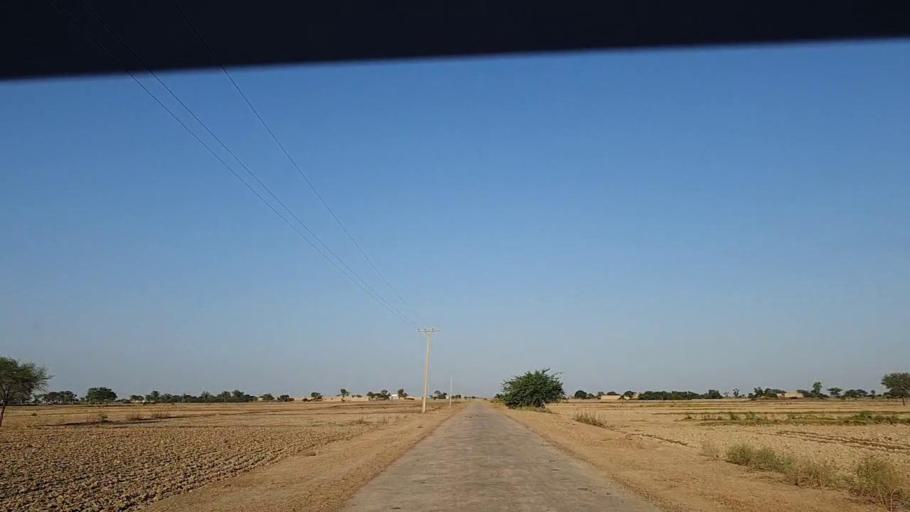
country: PK
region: Sindh
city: Johi
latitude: 26.7443
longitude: 67.6015
